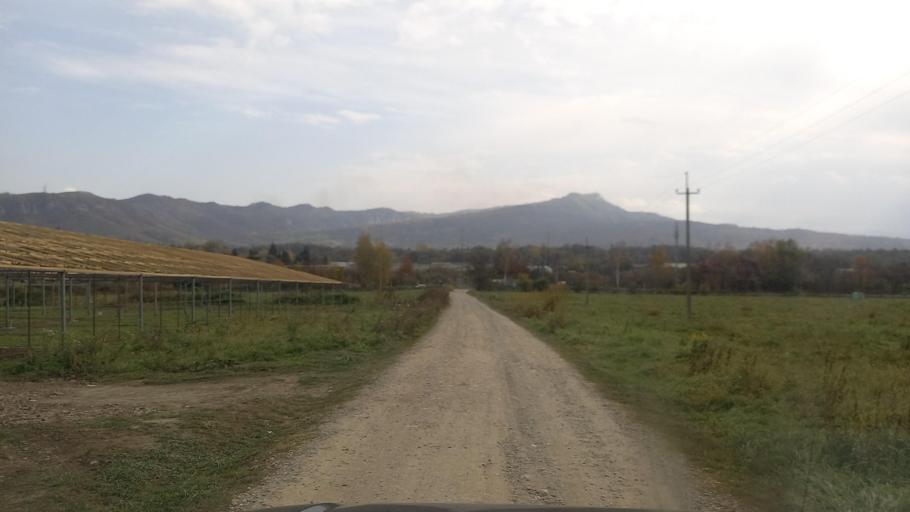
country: RU
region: Krasnodarskiy
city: Psebay
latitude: 44.1488
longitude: 40.8256
